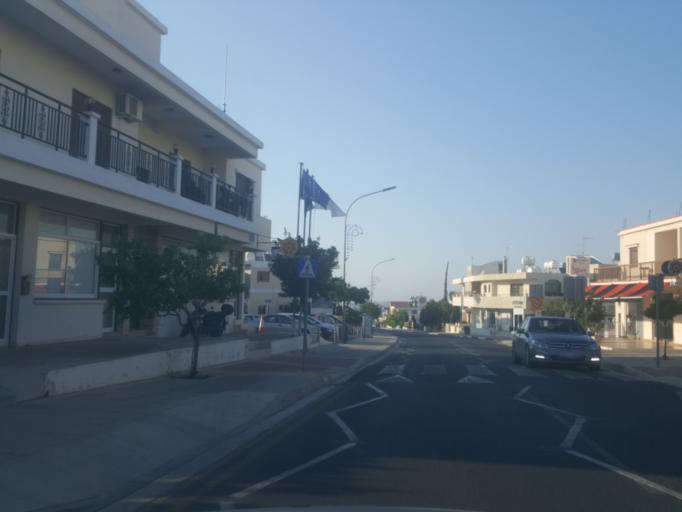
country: CY
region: Ammochostos
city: Deryneia
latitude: 35.0667
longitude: 33.9609
